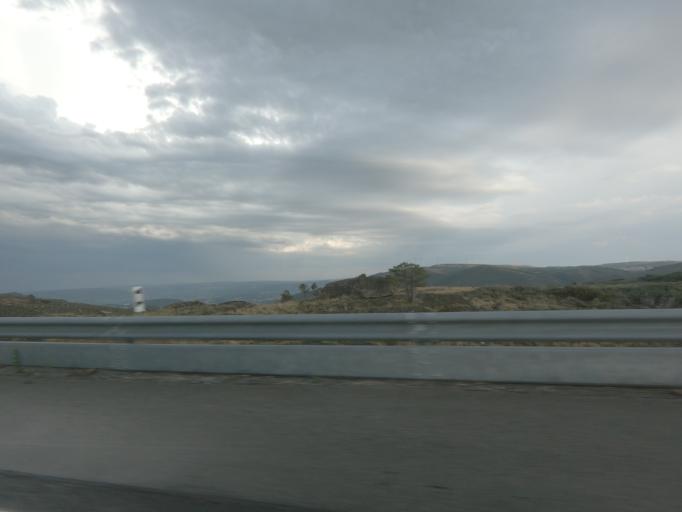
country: PT
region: Viseu
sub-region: Lamego
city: Lamego
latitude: 41.0354
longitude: -7.8624
